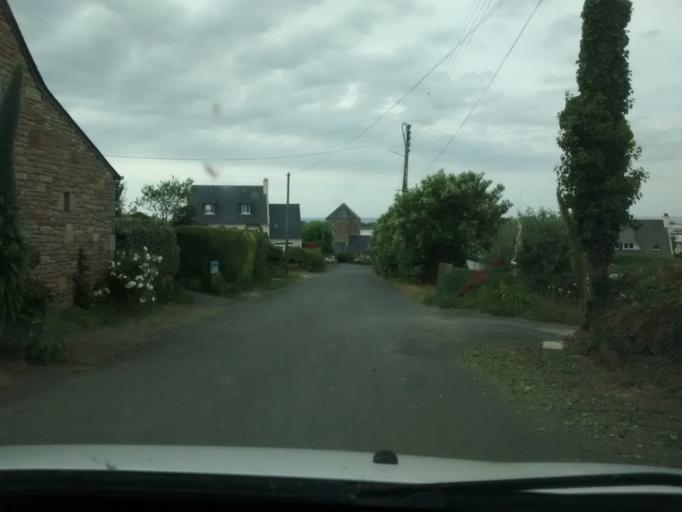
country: FR
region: Brittany
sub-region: Departement des Cotes-d'Armor
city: Penvenan
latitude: 48.8349
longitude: -3.2840
